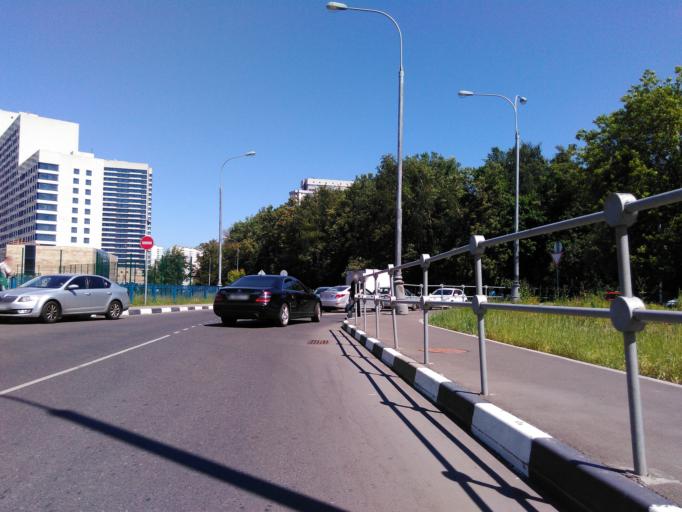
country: RU
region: Moskovskaya
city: Cheremushki
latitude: 55.6559
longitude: 37.5590
